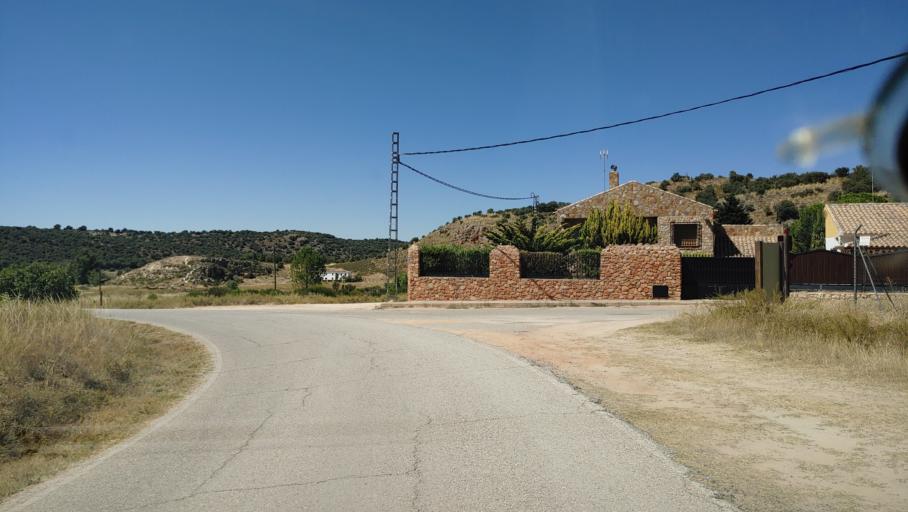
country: ES
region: Castille-La Mancha
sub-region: Provincia de Ciudad Real
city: Ruidera
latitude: 38.9266
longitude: -2.8296
